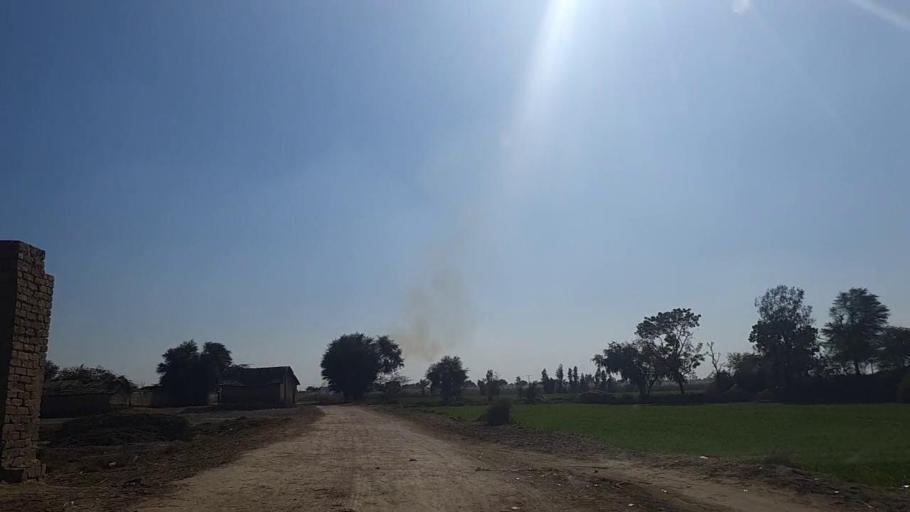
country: PK
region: Sindh
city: Sakrand
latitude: 26.2515
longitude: 68.1925
